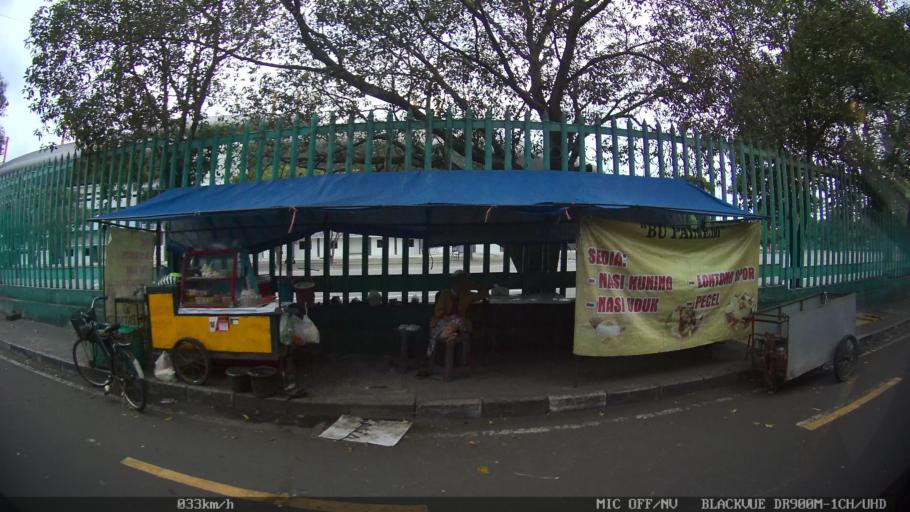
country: ID
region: Daerah Istimewa Yogyakarta
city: Yogyakarta
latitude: -7.7960
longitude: 110.3830
